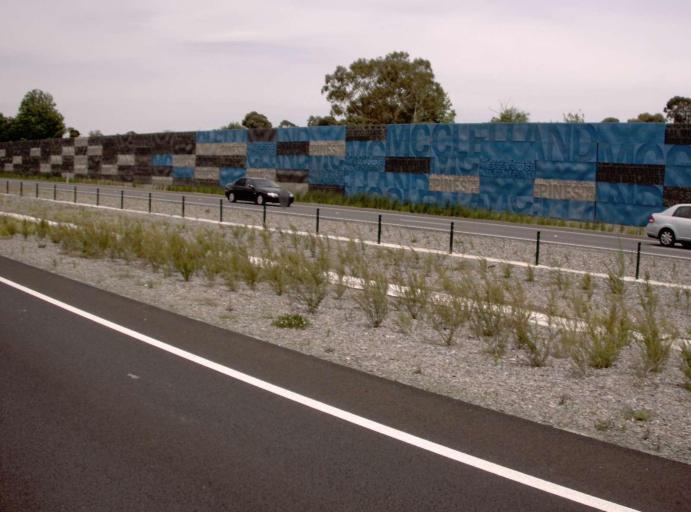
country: AU
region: Victoria
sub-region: Frankston
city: Langwarrin
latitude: -38.1438
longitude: 145.1731
